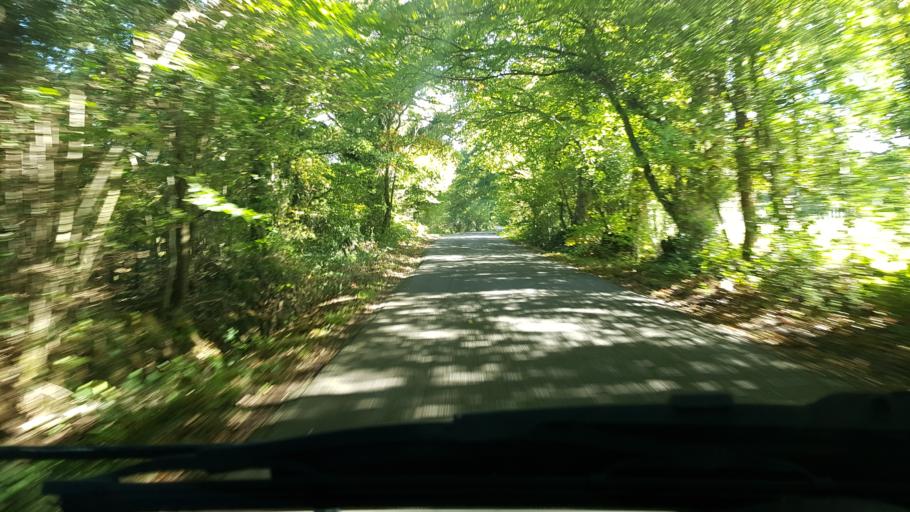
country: GB
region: England
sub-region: Surrey
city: Chiddingfold
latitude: 51.0877
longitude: -0.5905
